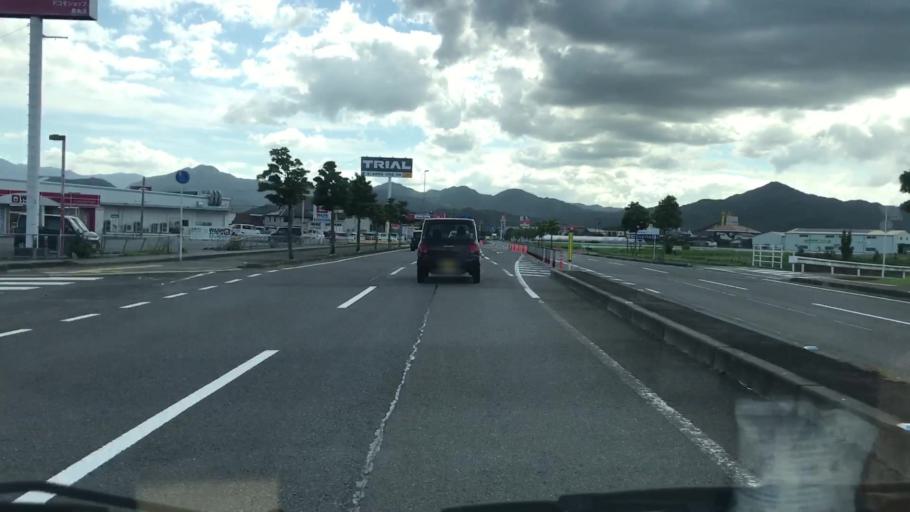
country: JP
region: Saga Prefecture
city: Kashima
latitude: 33.1243
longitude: 130.0986
